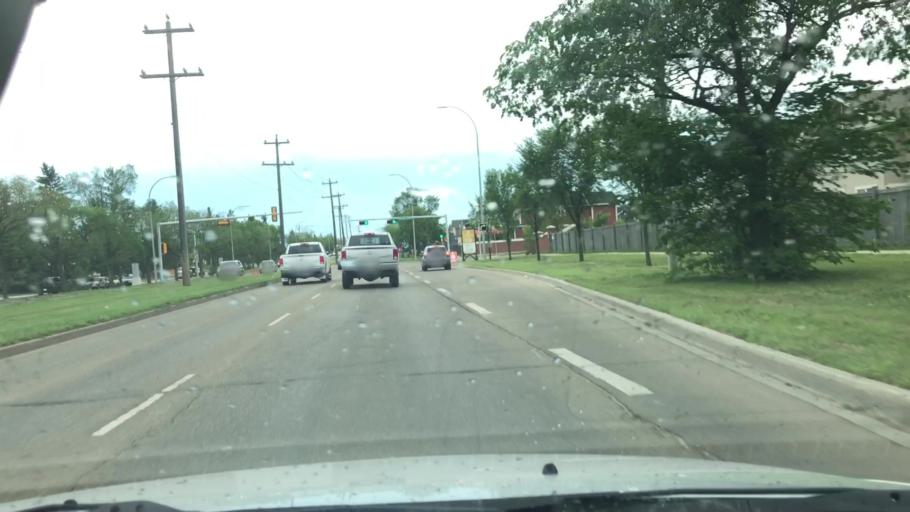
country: CA
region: Alberta
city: Edmonton
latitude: 53.5996
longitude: -113.5027
